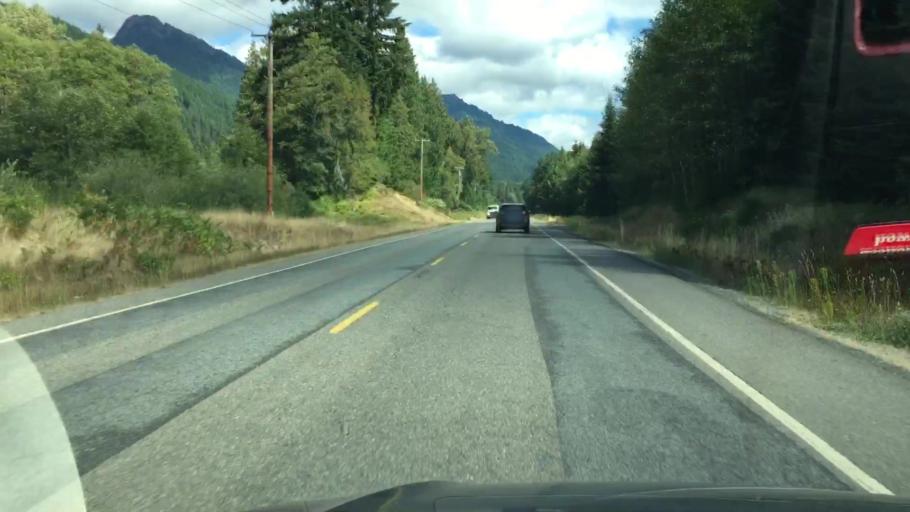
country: US
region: Washington
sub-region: Pierce County
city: Eatonville
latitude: 46.7571
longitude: -121.9961
